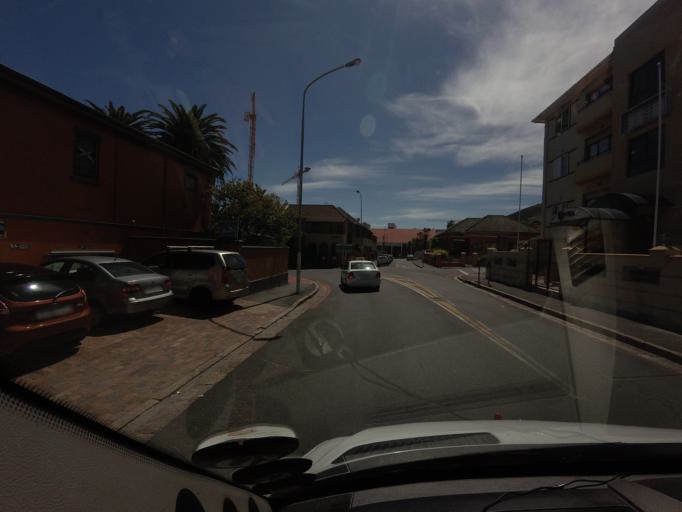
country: ZA
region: Western Cape
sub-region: City of Cape Town
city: Cape Town
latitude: -33.9236
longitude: 18.3805
